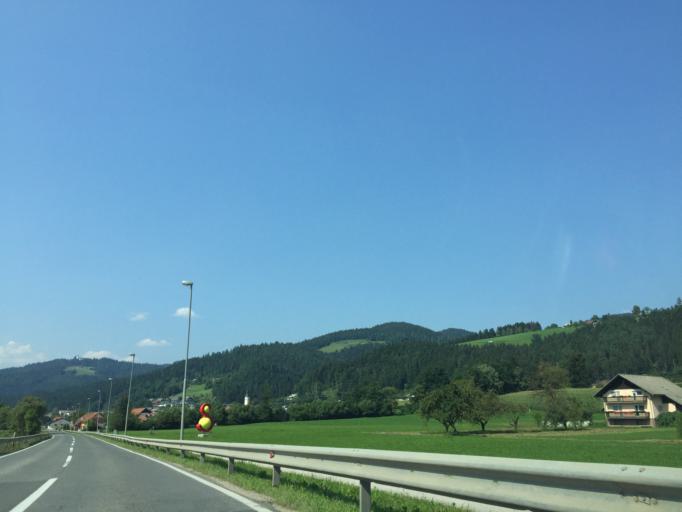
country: SI
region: Slovenj Gradec
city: Slovenj Gradec
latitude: 46.5195
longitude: 15.0861
